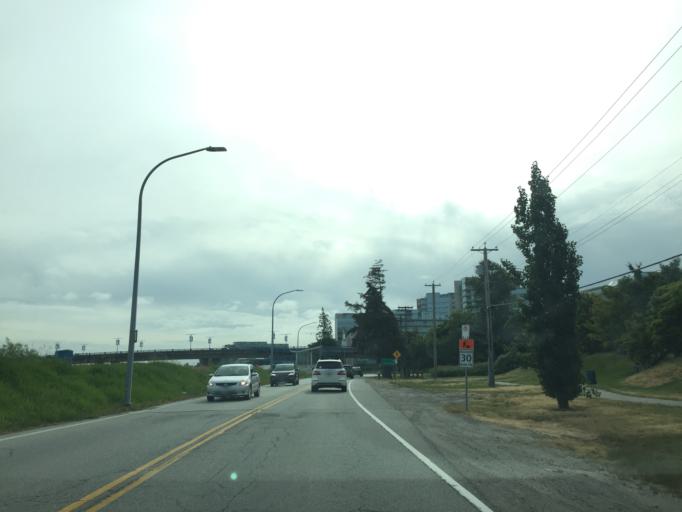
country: CA
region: British Columbia
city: Richmond
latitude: 49.1737
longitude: -123.1611
